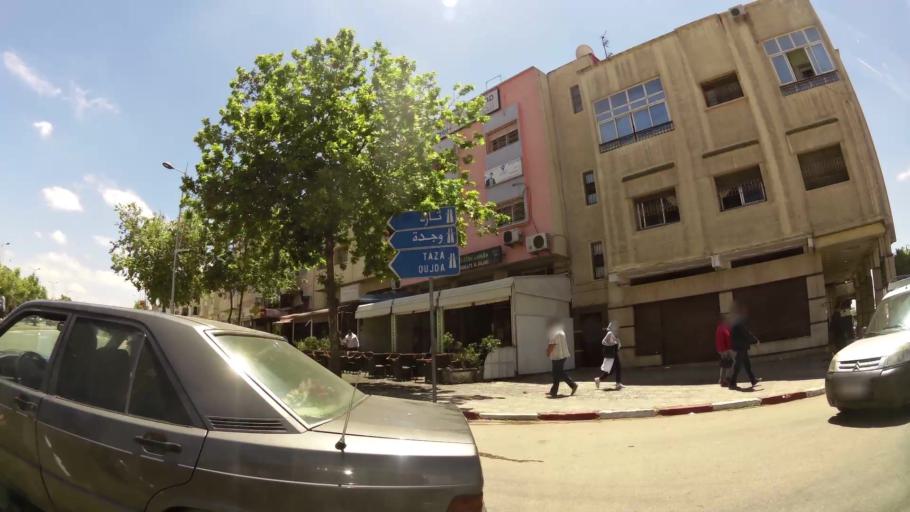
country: MA
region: Fes-Boulemane
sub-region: Fes
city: Fes
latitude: 34.0094
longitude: -4.9792
